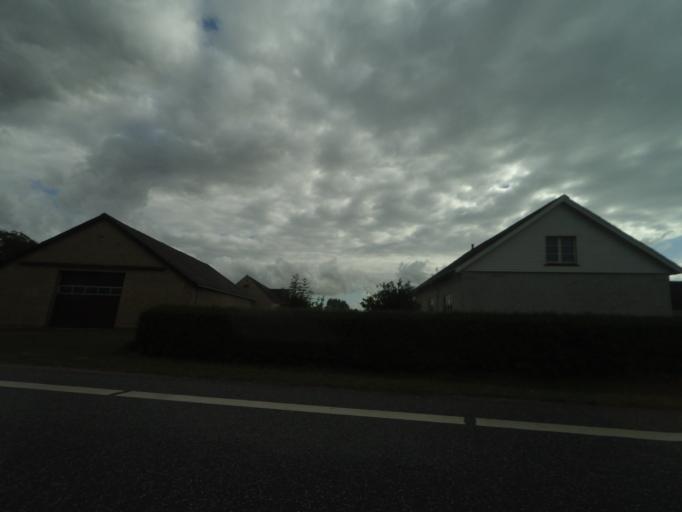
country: DK
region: South Denmark
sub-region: Middelfart Kommune
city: Norre Aby
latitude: 55.4654
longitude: 9.9132
